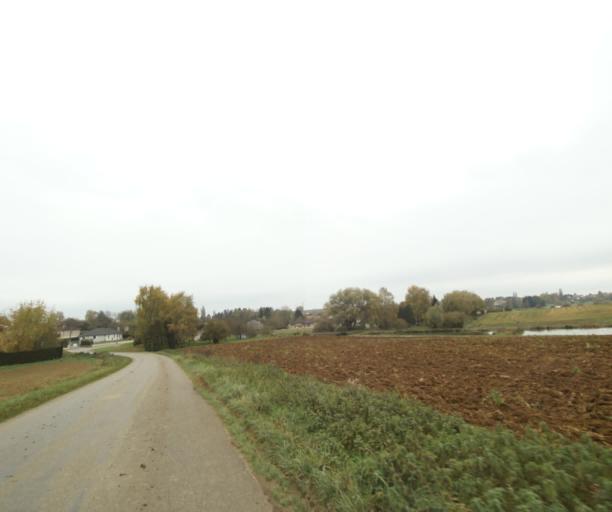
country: FR
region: Lorraine
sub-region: Departement de Meurthe-et-Moselle
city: Briey
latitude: 49.2533
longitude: 5.9092
